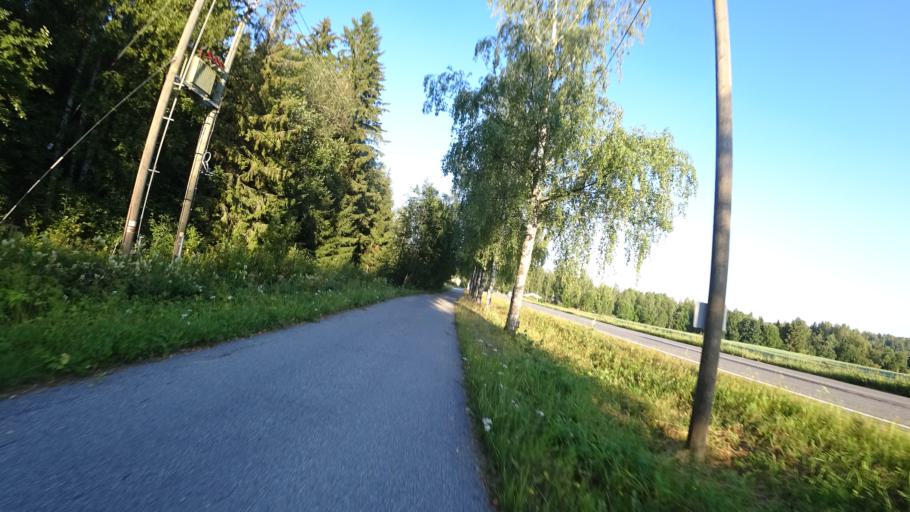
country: FI
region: Pirkanmaa
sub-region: Tampere
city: Nokia
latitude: 61.4703
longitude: 23.3906
